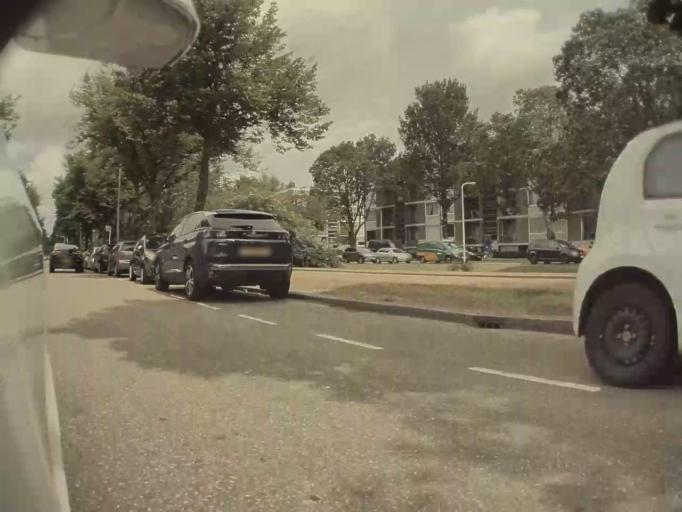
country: NL
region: South Holland
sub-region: Gemeente Westland
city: Kwintsheul
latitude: 52.0367
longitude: 4.2712
